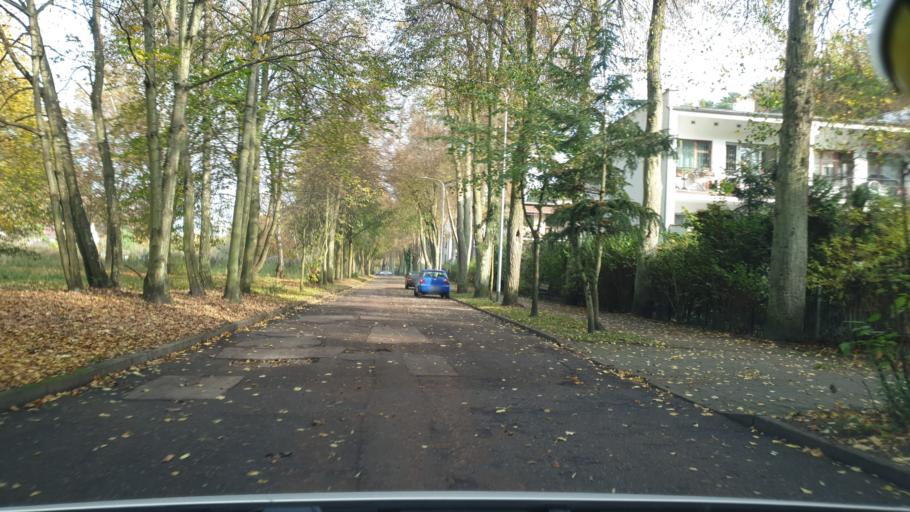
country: PL
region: Pomeranian Voivodeship
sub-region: Sopot
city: Sopot
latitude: 54.3876
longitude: 18.5641
